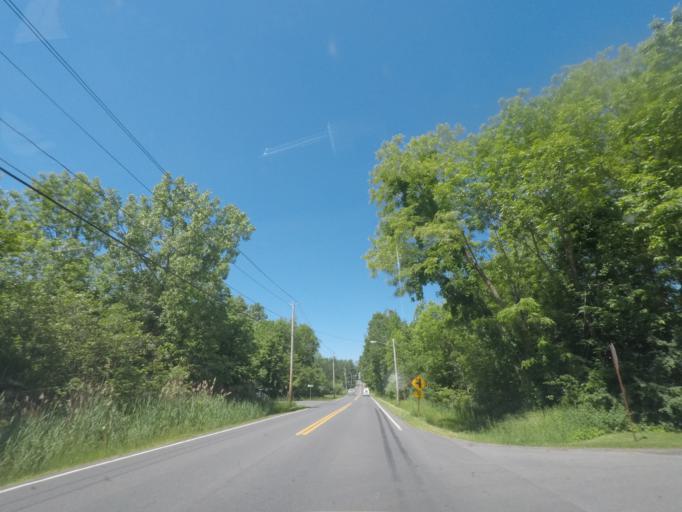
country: US
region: New York
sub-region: Saratoga County
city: Country Knolls
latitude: 42.8581
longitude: -73.8251
